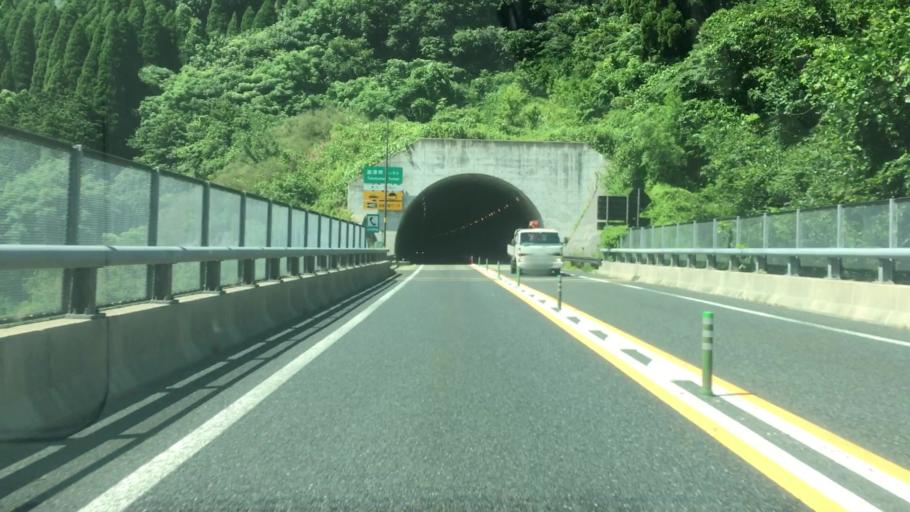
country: JP
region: Tottori
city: Tottori
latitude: 35.3807
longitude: 134.2049
